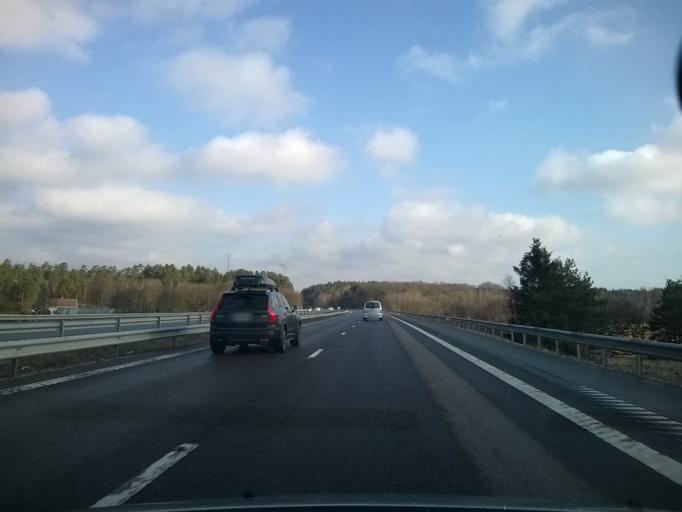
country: SE
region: Vaestra Goetaland
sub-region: Stenungsunds Kommun
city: Stora Hoga
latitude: 57.9988
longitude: 11.8437
